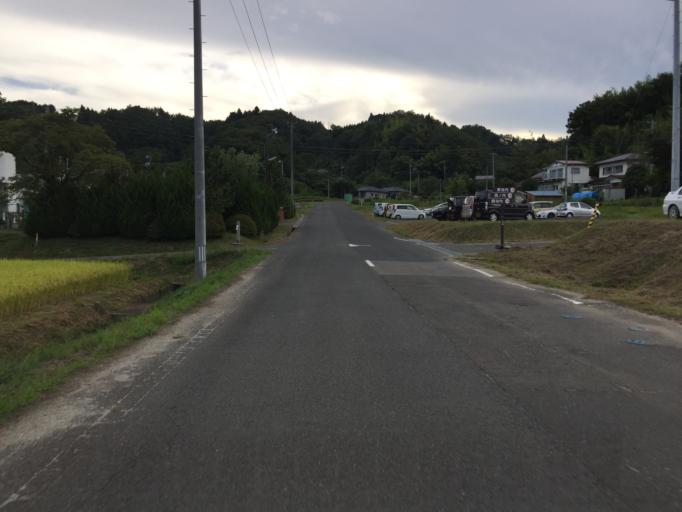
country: JP
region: Fukushima
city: Fukushima-shi
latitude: 37.6774
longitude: 140.5788
